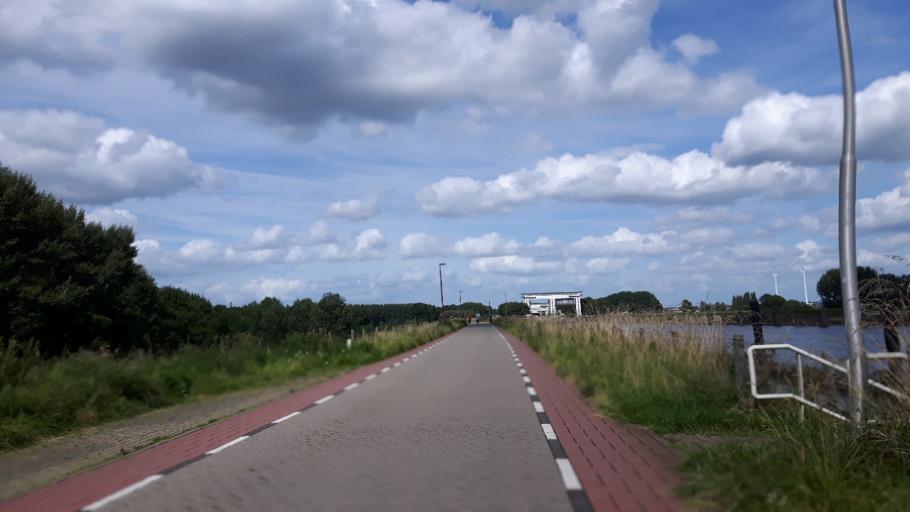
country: NL
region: Utrecht
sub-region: Gemeente Vianen
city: Vianen
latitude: 52.0065
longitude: 5.1041
